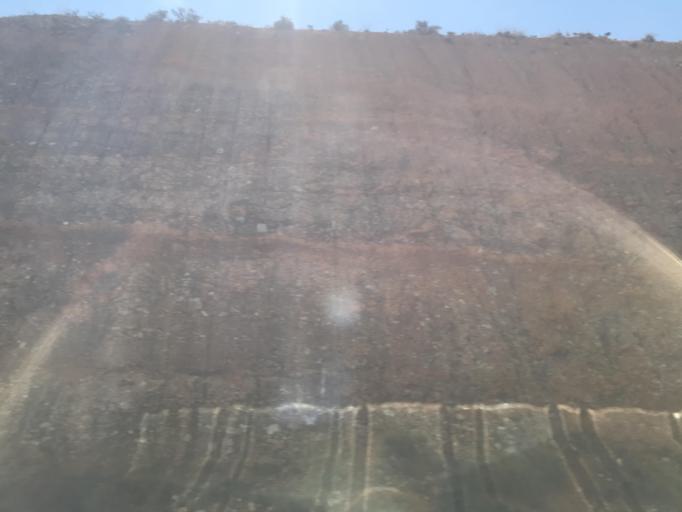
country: ES
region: Castille and Leon
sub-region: Provincia de Soria
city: Arcos de Jalon
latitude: 41.1774
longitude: -2.2291
